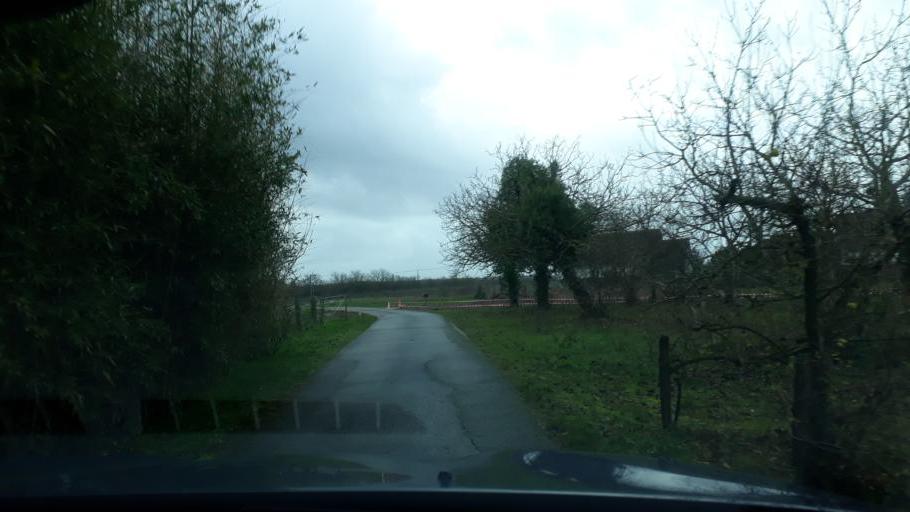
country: FR
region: Centre
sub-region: Departement du Loiret
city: Mareau-aux-Pres
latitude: 47.8332
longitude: 1.8013
